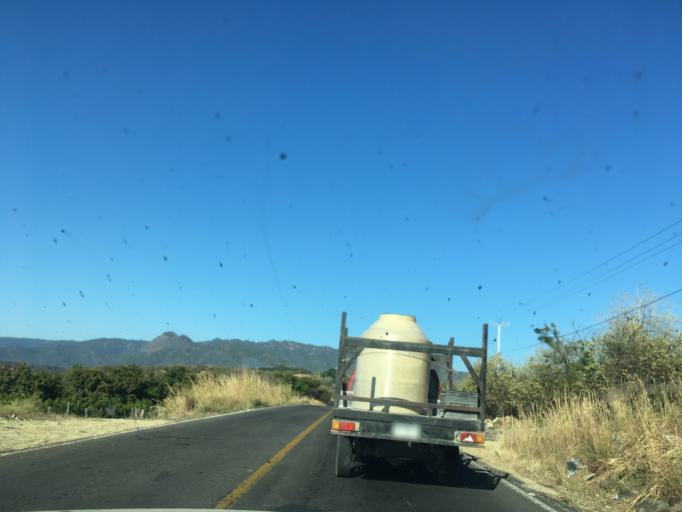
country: MX
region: Michoacan
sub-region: Gabriel Zamora
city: Lombardia
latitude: 19.1900
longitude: -102.0608
